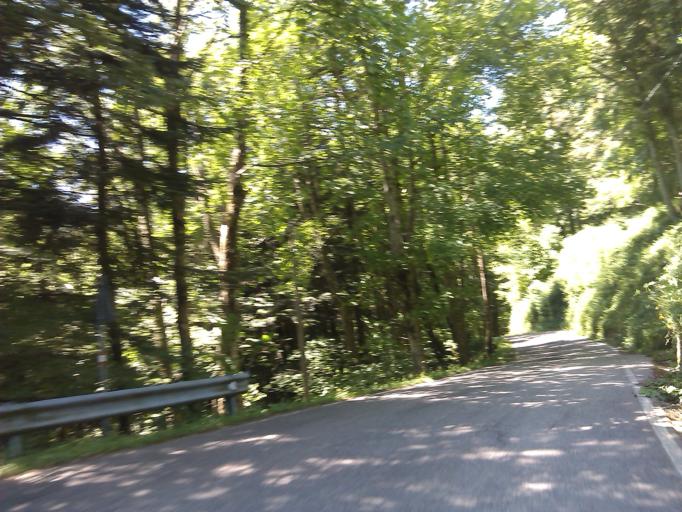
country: IT
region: Tuscany
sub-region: Provincia di Prato
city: Cantagallo
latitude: 44.0076
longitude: 11.0148
